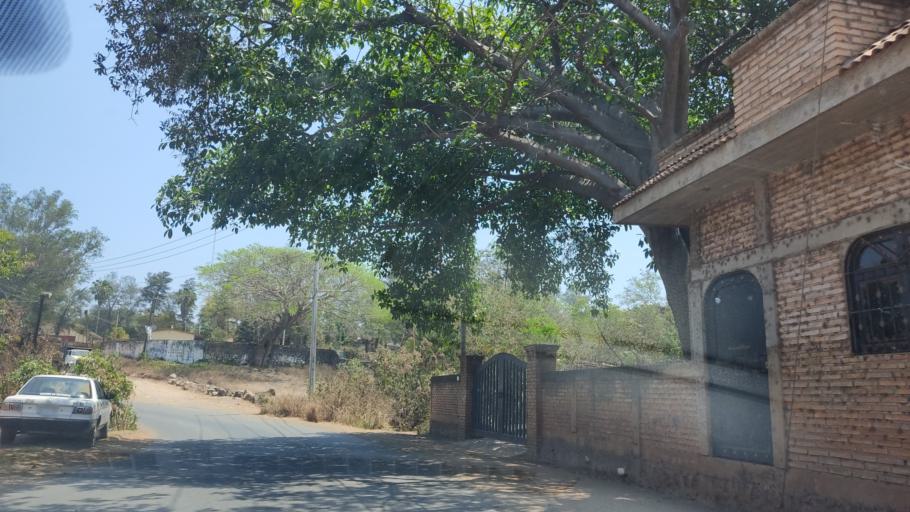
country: MX
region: Nayarit
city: Puga
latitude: 21.5856
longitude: -104.8129
